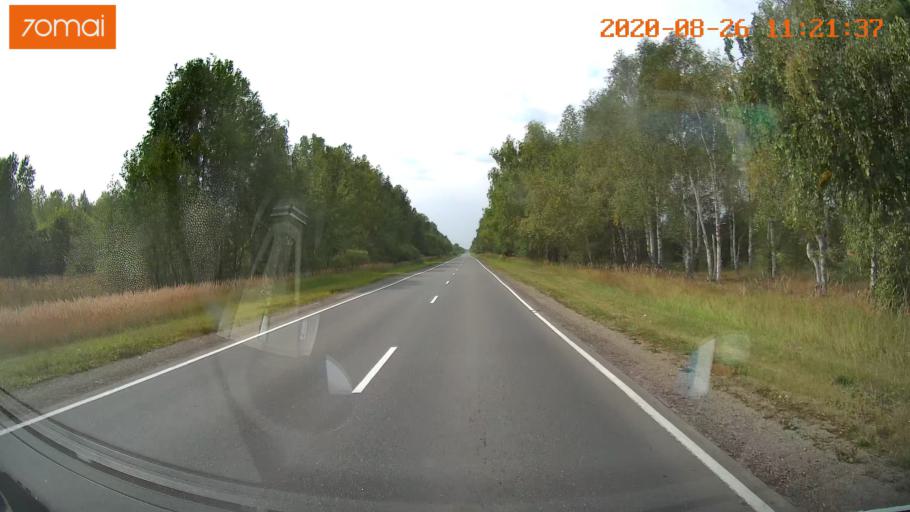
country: RU
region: Rjazan
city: Shilovo
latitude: 54.3741
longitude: 41.0417
